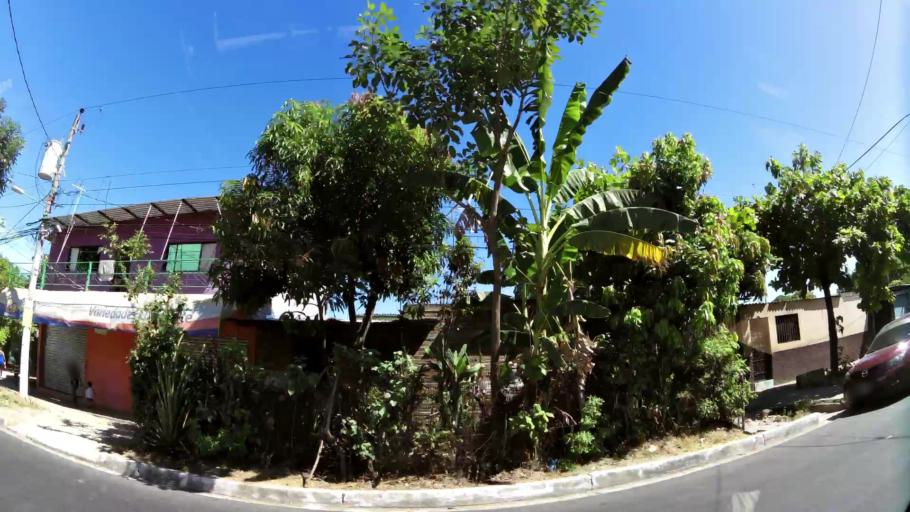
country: SV
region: San Salvador
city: Apopa
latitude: 13.8089
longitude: -89.1794
